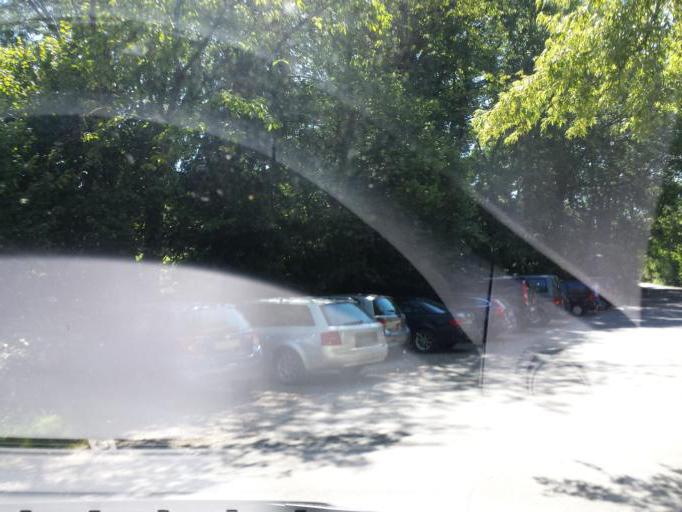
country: DE
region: Baden-Wuerttemberg
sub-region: Tuebingen Region
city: Uberlingen
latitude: 47.7847
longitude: 9.1994
